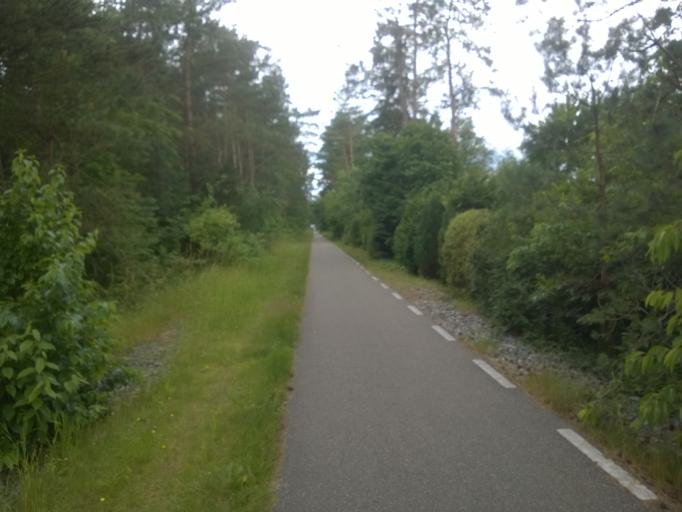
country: DK
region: Central Jutland
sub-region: Silkeborg Kommune
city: Svejbaek
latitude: 56.1710
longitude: 9.6145
